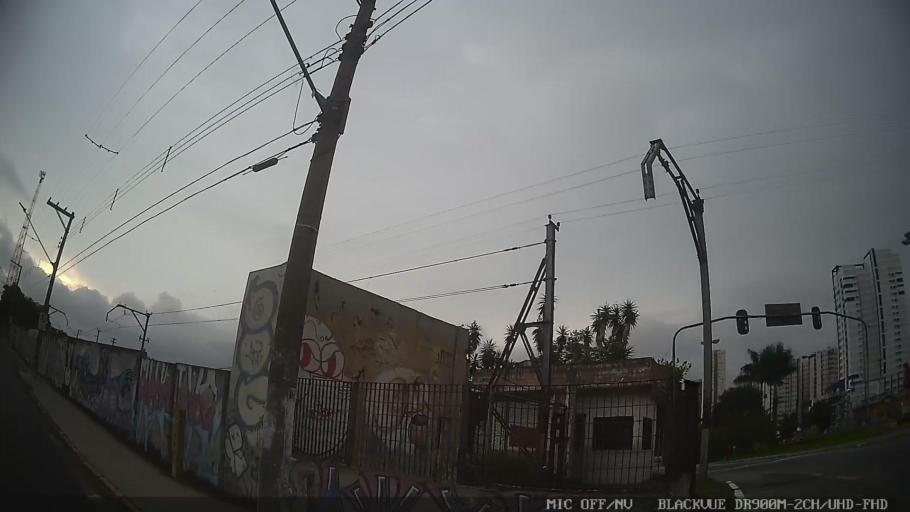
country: BR
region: Sao Paulo
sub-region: Mogi das Cruzes
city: Mogi das Cruzes
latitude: -23.5153
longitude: -46.1847
